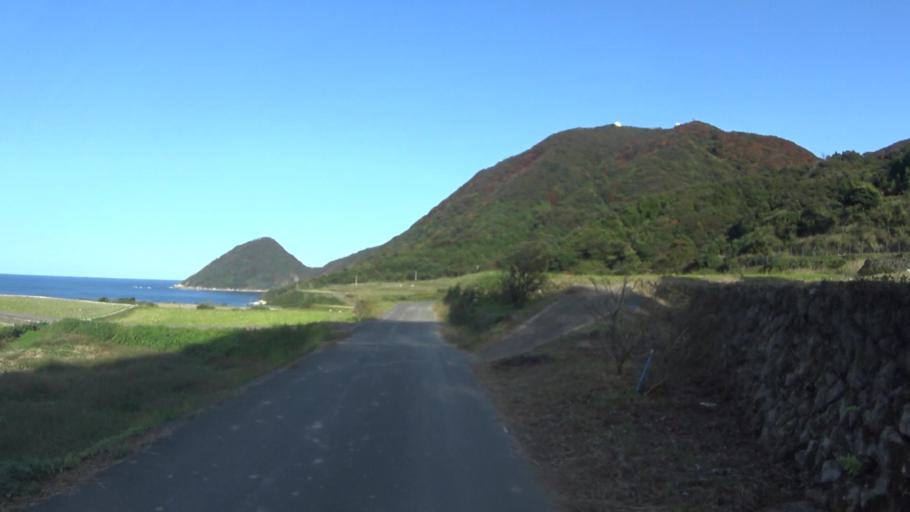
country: JP
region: Kyoto
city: Miyazu
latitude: 35.7609
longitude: 135.2046
